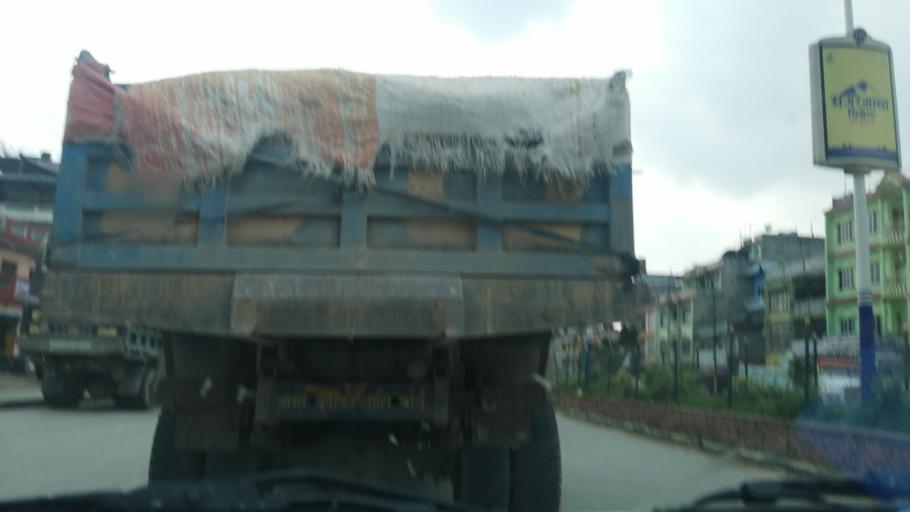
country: NP
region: Western Region
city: Butwal
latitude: 27.7060
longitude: 83.4674
